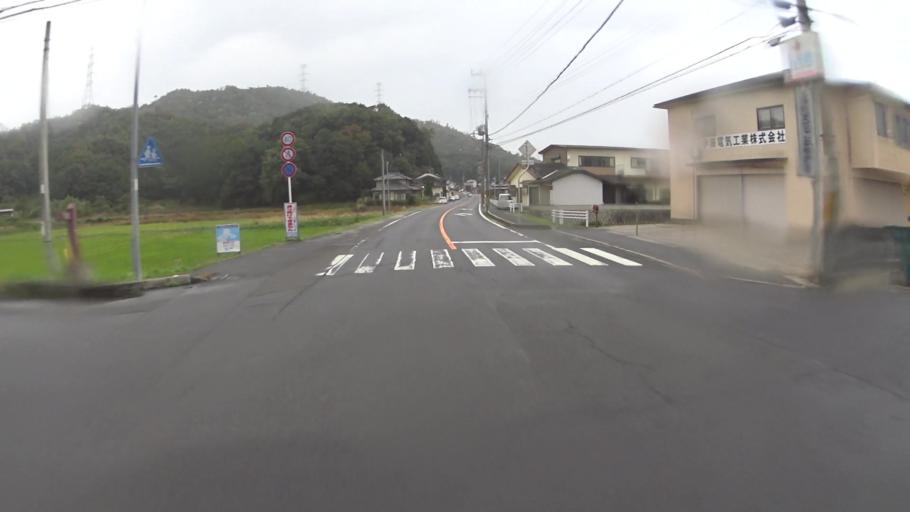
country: JP
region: Kyoto
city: Miyazu
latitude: 35.5524
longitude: 135.2344
